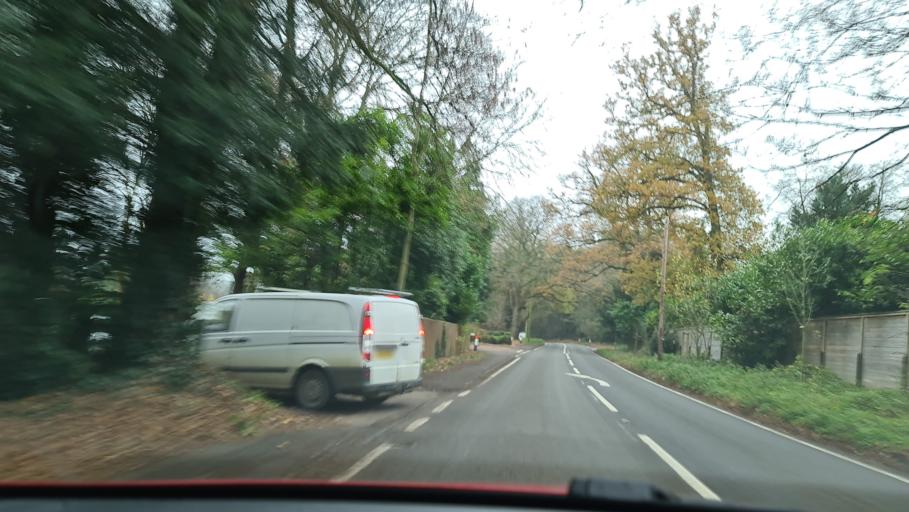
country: GB
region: England
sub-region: Buckinghamshire
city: Beaconsfield
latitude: 51.6256
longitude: -0.6554
